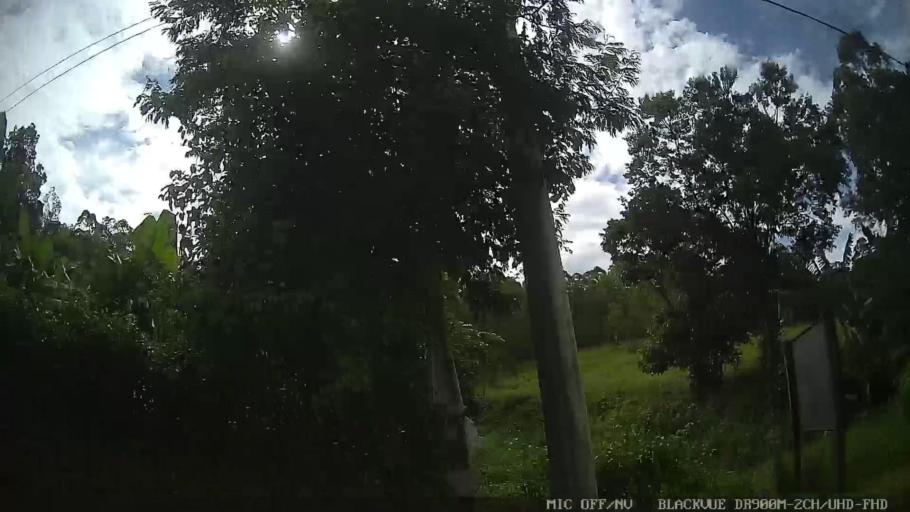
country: BR
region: Sao Paulo
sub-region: Santa Branca
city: Santa Branca
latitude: -23.5263
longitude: -45.8985
